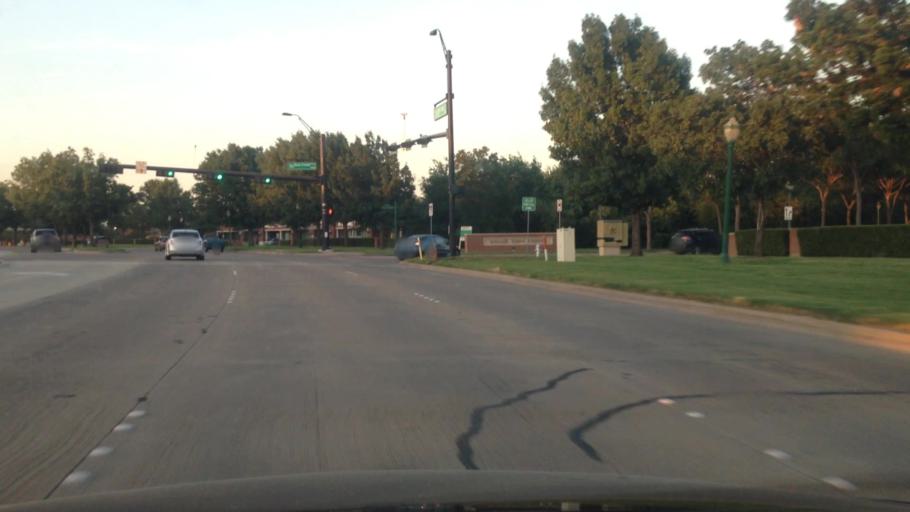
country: US
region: Texas
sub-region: Tarrant County
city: Keller
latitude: 32.9309
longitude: -97.2301
